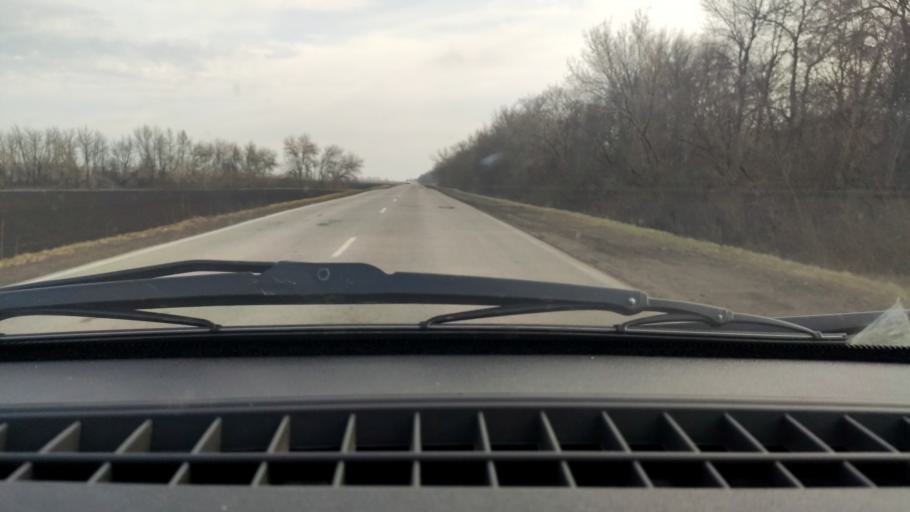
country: RU
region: Bashkortostan
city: Chishmy
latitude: 54.4616
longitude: 55.2558
